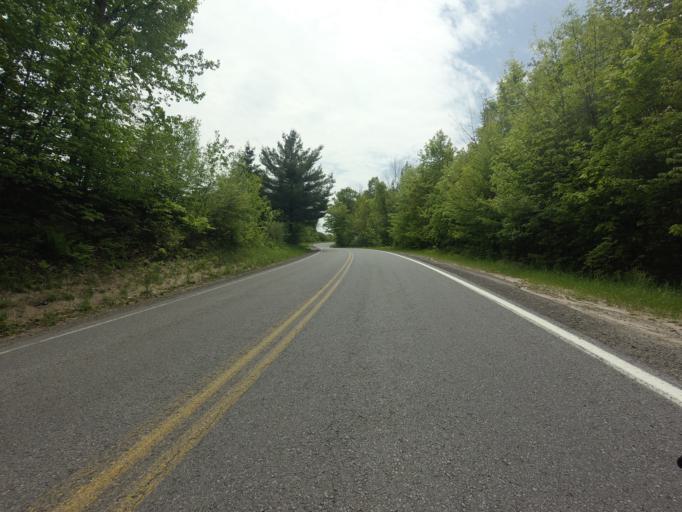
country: US
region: New York
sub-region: St. Lawrence County
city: Hannawa Falls
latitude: 44.5474
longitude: -75.0060
